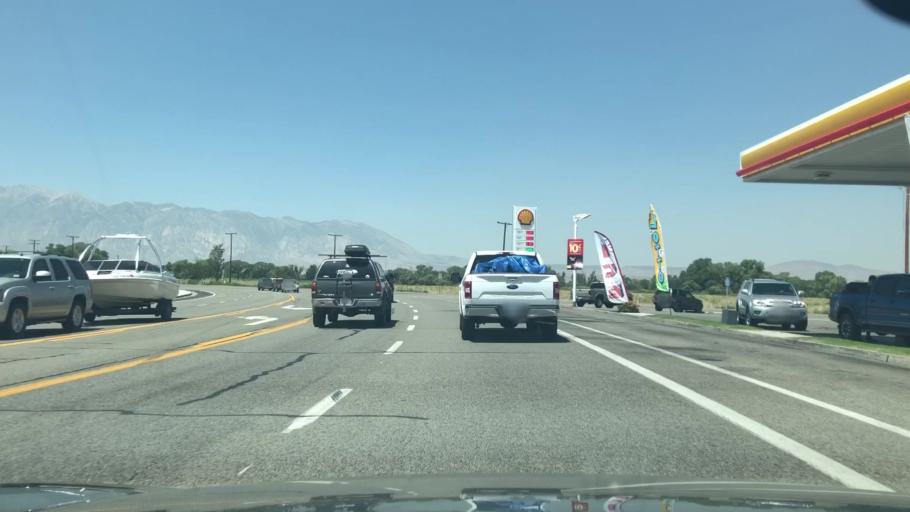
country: US
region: California
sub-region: Inyo County
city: Bishop
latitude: 37.3724
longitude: -118.3986
